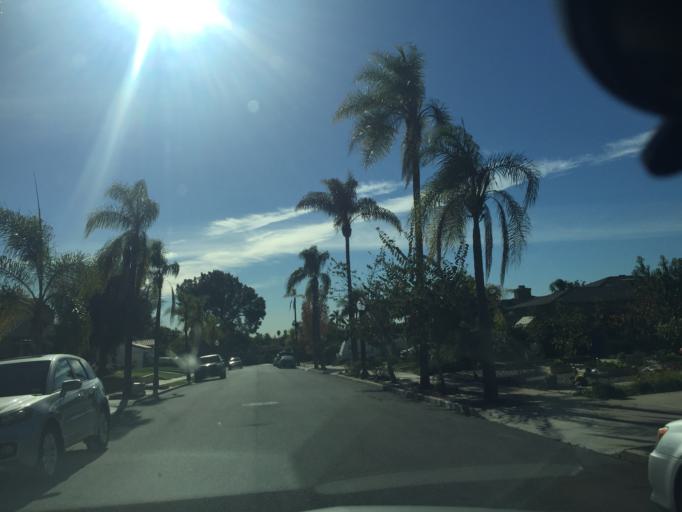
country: US
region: California
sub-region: San Diego County
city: Lemon Grove
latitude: 32.7627
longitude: -117.0944
